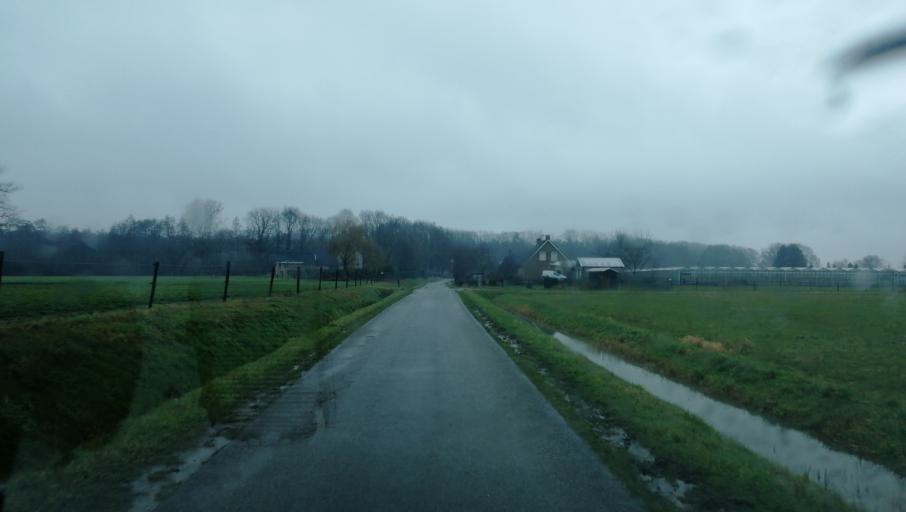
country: NL
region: Limburg
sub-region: Gemeente Venlo
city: Tegelen
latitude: 51.3593
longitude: 6.1077
